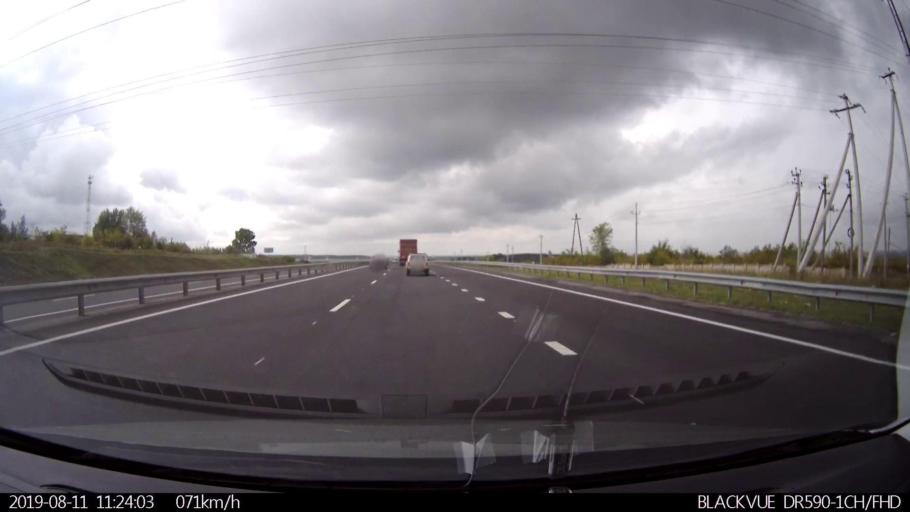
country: RU
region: Ulyanovsk
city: Krasnyy Gulyay
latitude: 54.1305
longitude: 48.2459
